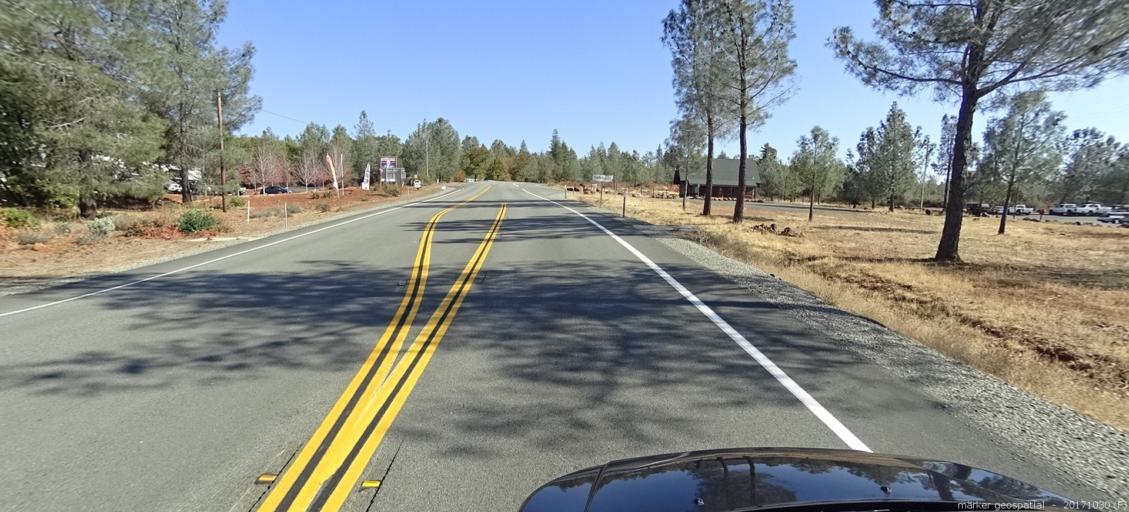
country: US
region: California
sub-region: Shasta County
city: Shingletown
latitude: 40.5015
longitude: -121.9938
